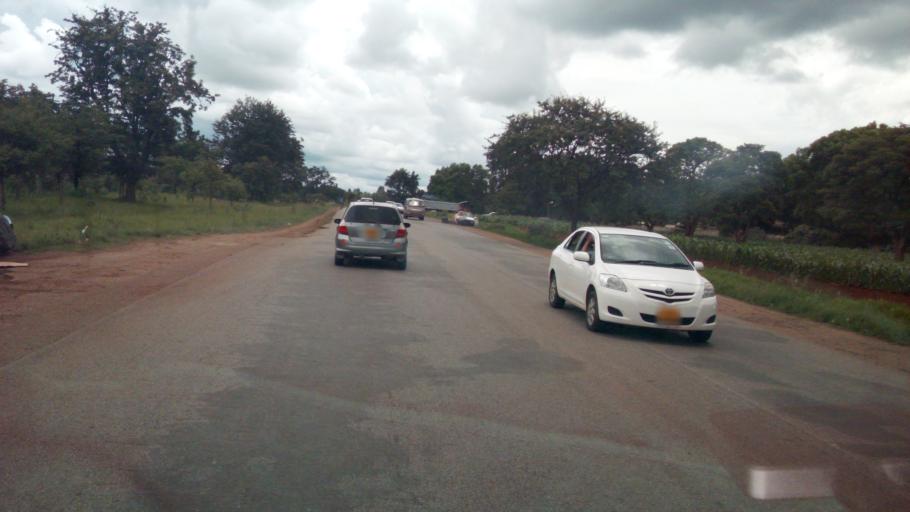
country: ZW
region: Harare
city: Harare
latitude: -17.7869
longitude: 30.9906
